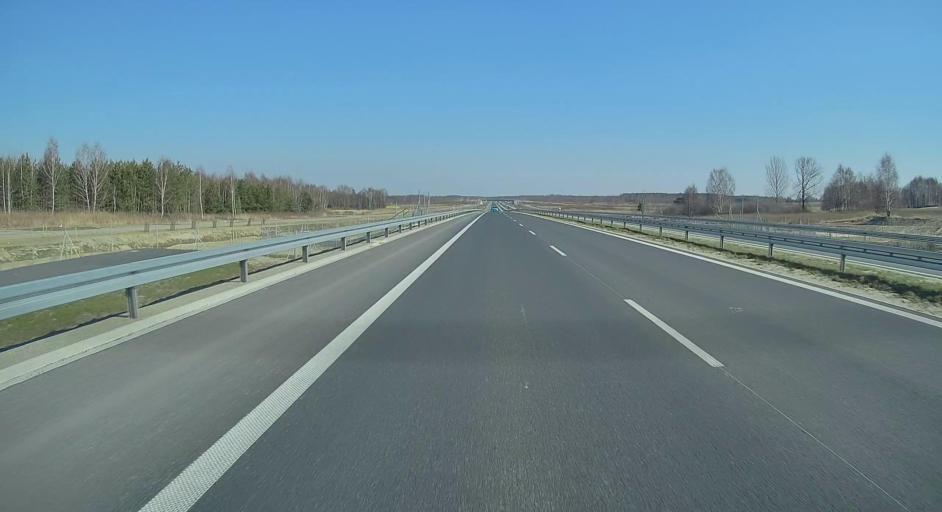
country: PL
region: Subcarpathian Voivodeship
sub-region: Powiat rzeszowski
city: Gorno
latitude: 50.3074
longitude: 22.1457
